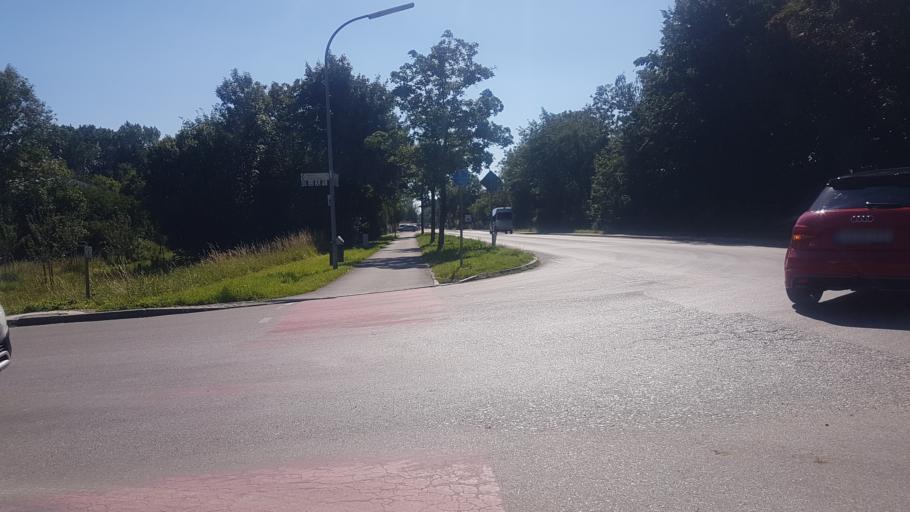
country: DE
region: Bavaria
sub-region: Upper Bavaria
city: Bergheim
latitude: 48.7377
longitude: 11.2259
